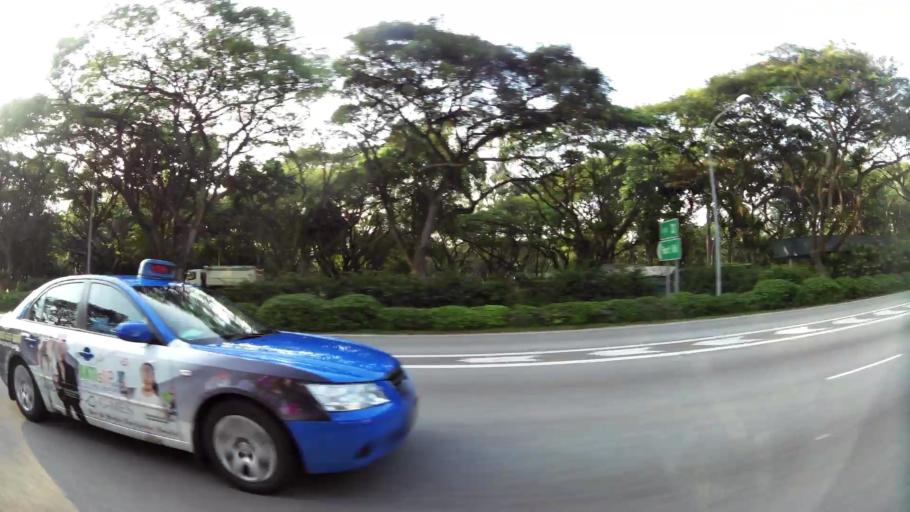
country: SG
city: Singapore
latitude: 1.2956
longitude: 103.8882
